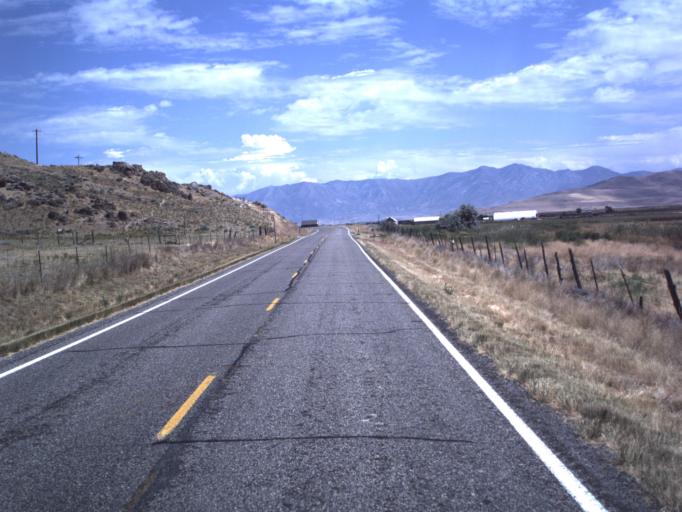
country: US
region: Utah
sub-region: Box Elder County
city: Tremonton
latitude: 41.6220
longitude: -112.3524
